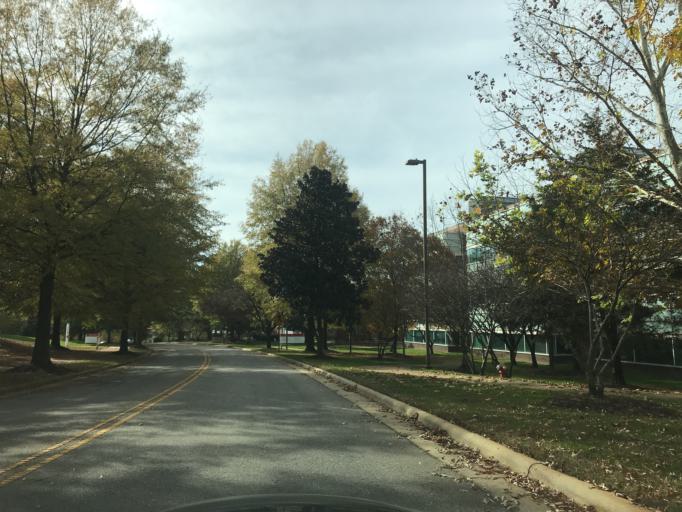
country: US
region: North Carolina
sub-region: Wake County
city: West Raleigh
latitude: 35.7751
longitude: -78.6749
